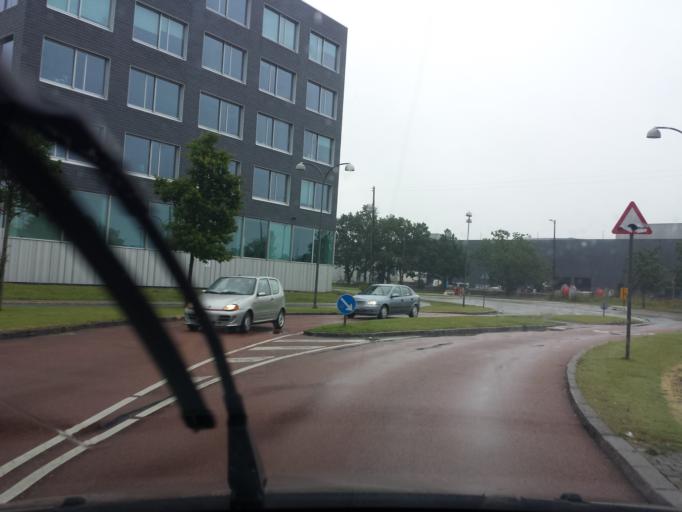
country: DK
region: Capital Region
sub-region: Herlev Kommune
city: Herlev
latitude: 55.7188
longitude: 12.4458
